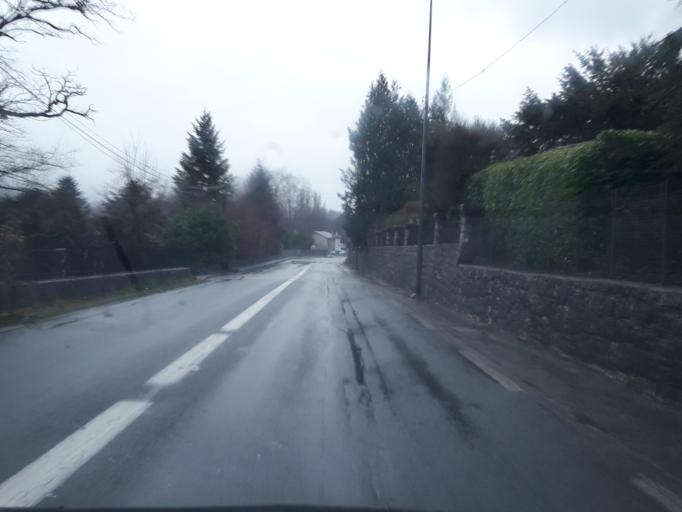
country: FR
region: Rhone-Alpes
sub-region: Departement de la Savoie
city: Le Bourget-du-Lac
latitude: 45.6561
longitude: 5.8575
